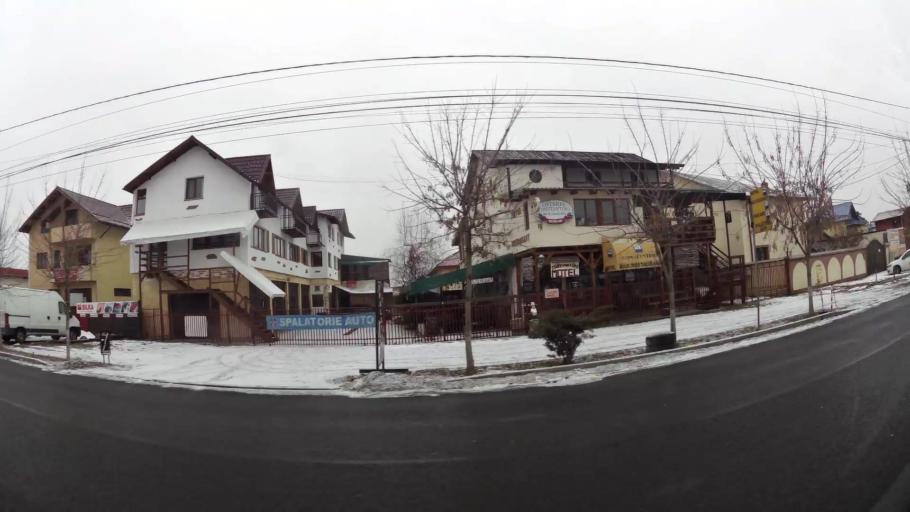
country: RO
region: Dambovita
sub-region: Municipiul Targoviste
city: Targoviste
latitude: 44.9350
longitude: 25.4400
